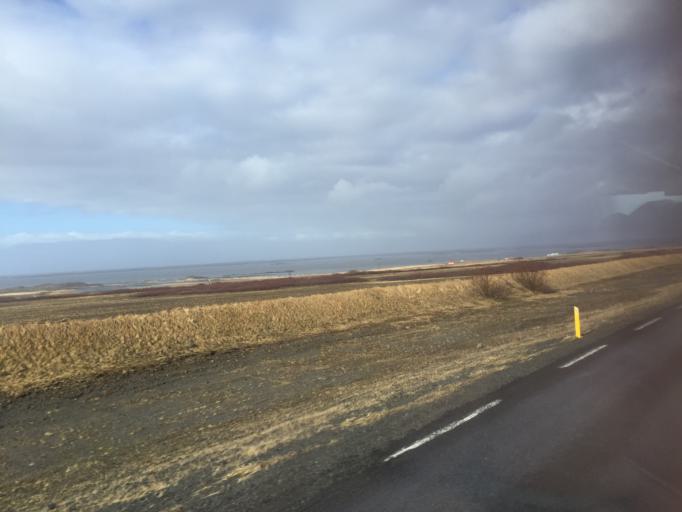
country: IS
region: West
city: Borgarnes
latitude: 64.4563
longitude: -21.9609
